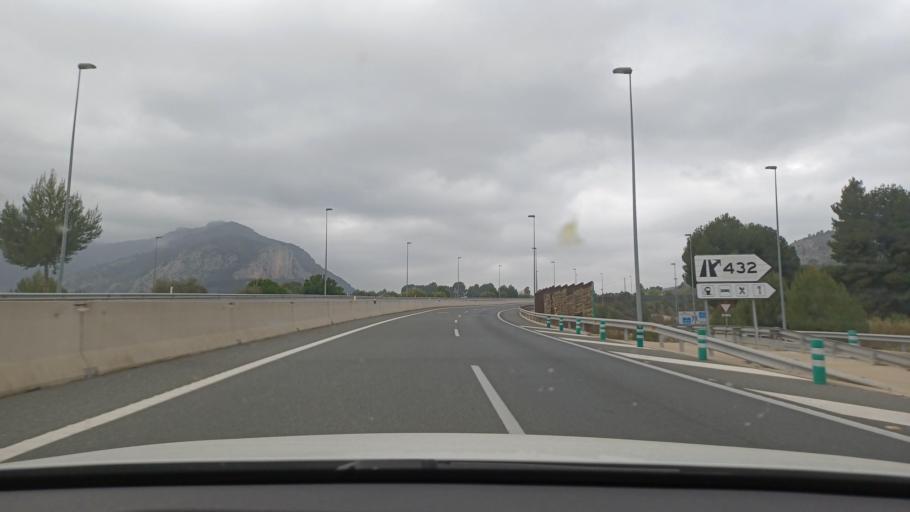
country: ES
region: Valencia
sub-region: Provincia de Alicante
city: Muro del Alcoy
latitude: 38.7945
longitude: -0.4462
